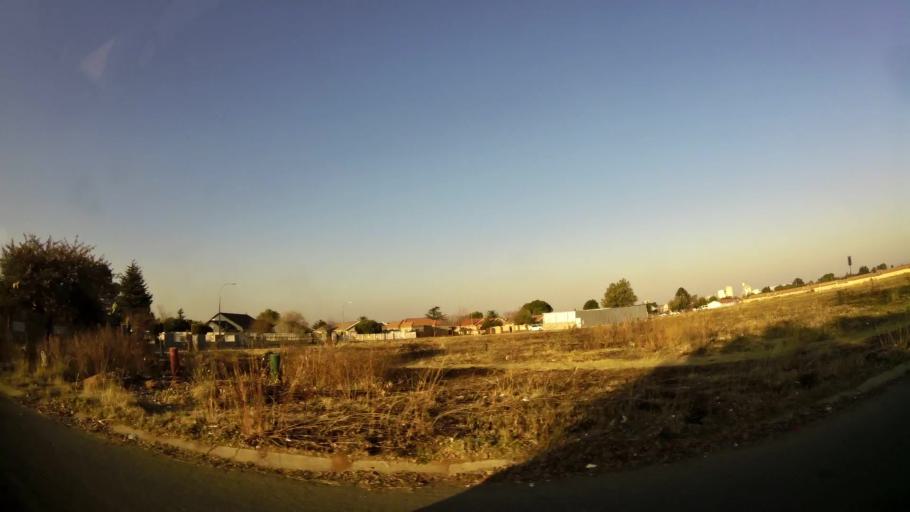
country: ZA
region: Gauteng
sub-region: West Rand District Municipality
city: Randfontein
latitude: -26.2060
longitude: 27.6520
